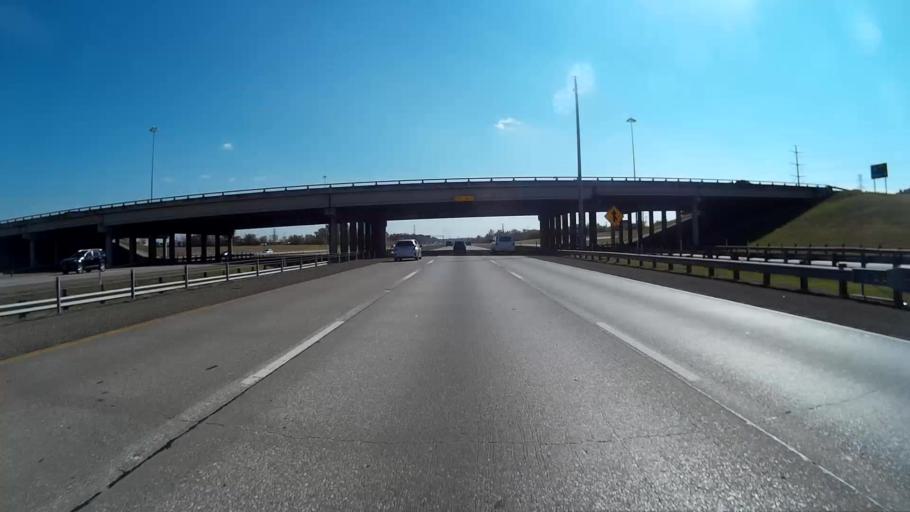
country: US
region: Texas
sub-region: Dallas County
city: Hutchins
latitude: 32.7016
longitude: -96.7534
